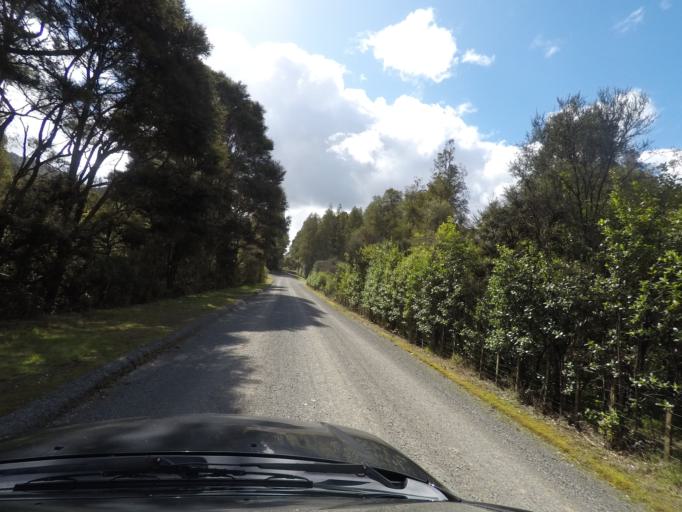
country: NZ
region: Auckland
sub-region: Auckland
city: Red Hill
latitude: -37.0918
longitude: 175.1536
